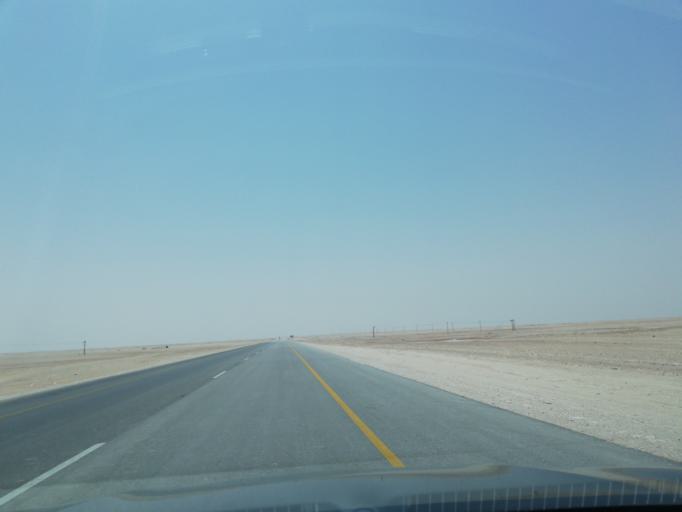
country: OM
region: Al Wusta
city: Hayma'
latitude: 19.6173
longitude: 55.7235
